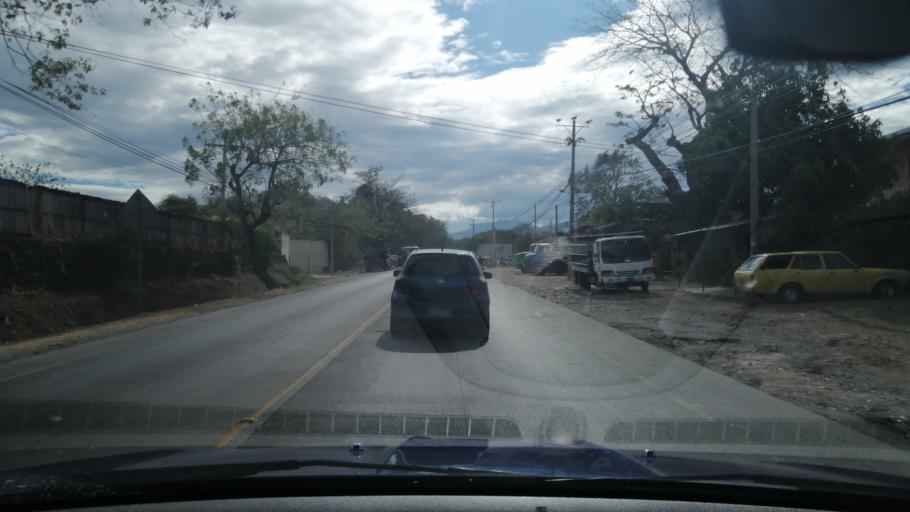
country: SV
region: Santa Ana
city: Santa Ana
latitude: 14.0157
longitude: -89.5390
